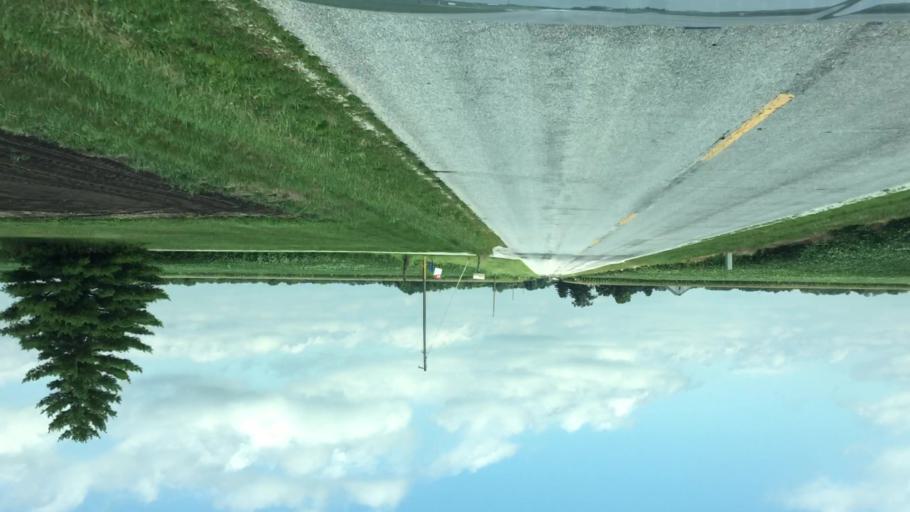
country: US
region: Illinois
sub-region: Hancock County
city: Nauvoo
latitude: 40.5121
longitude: -91.3082
